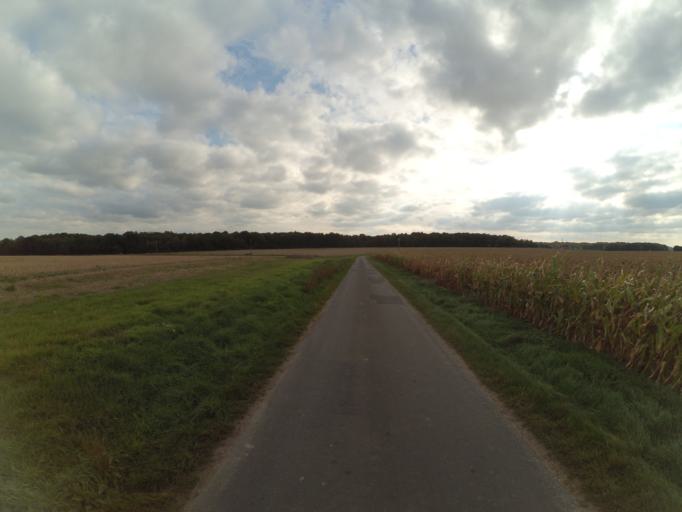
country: FR
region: Centre
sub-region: Departement d'Indre-et-Loire
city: Nazelles-Negron
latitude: 47.4746
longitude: 0.9428
